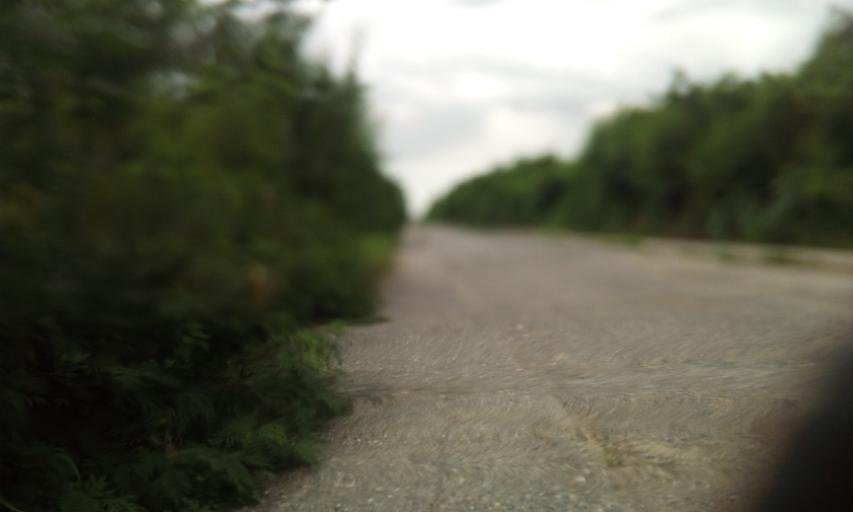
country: TH
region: Pathum Thani
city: Nong Suea
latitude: 14.0699
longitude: 100.8353
